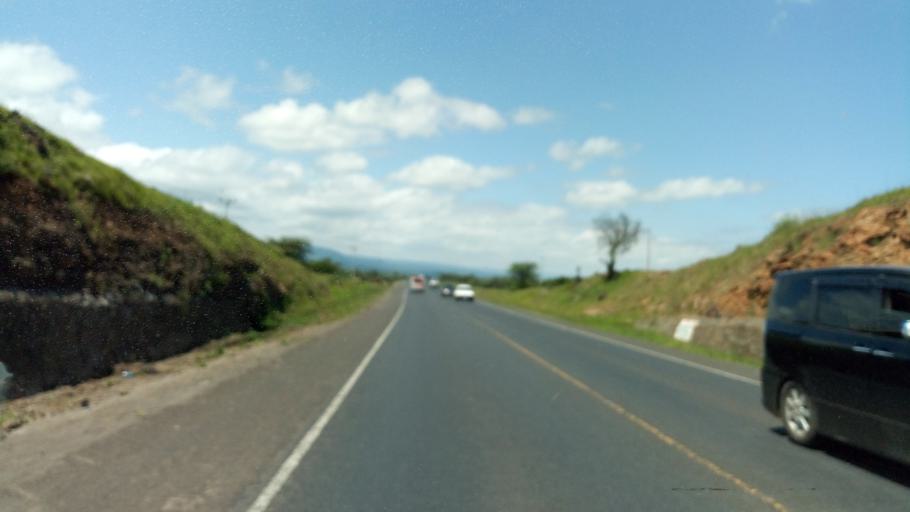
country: KE
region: Nakuru
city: Naivasha
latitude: -0.5440
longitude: 36.3409
